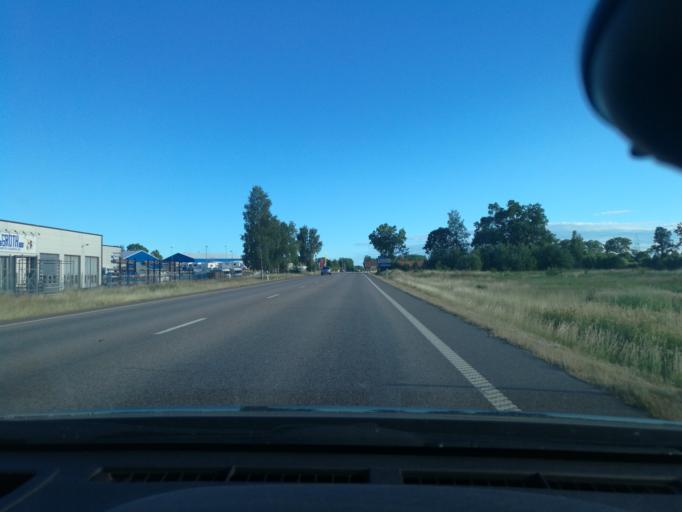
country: SE
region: Kalmar
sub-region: Monsteras Kommun
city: Moensteras
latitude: 57.0385
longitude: 16.4348
